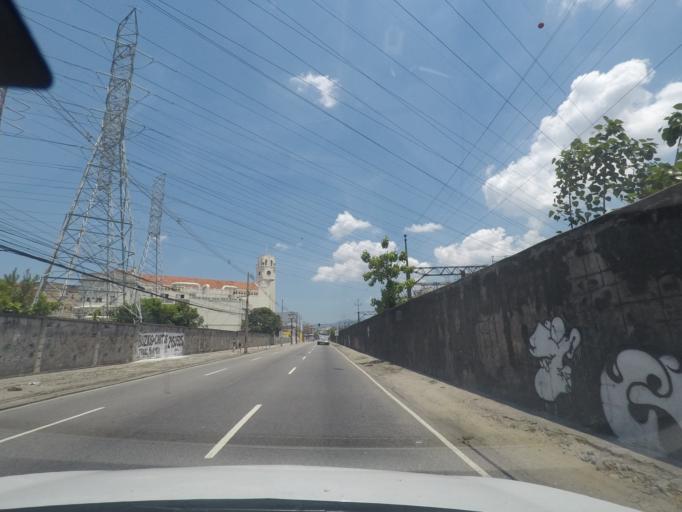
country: BR
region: Rio de Janeiro
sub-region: Sao Joao De Meriti
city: Sao Joao de Meriti
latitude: -22.8787
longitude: -43.3338
